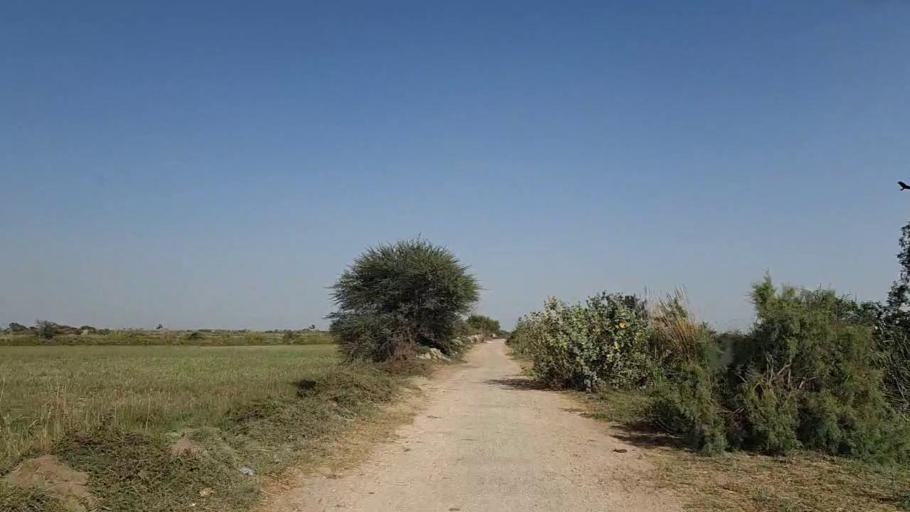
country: PK
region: Sindh
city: Chuhar Jamali
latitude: 24.4816
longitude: 68.1098
